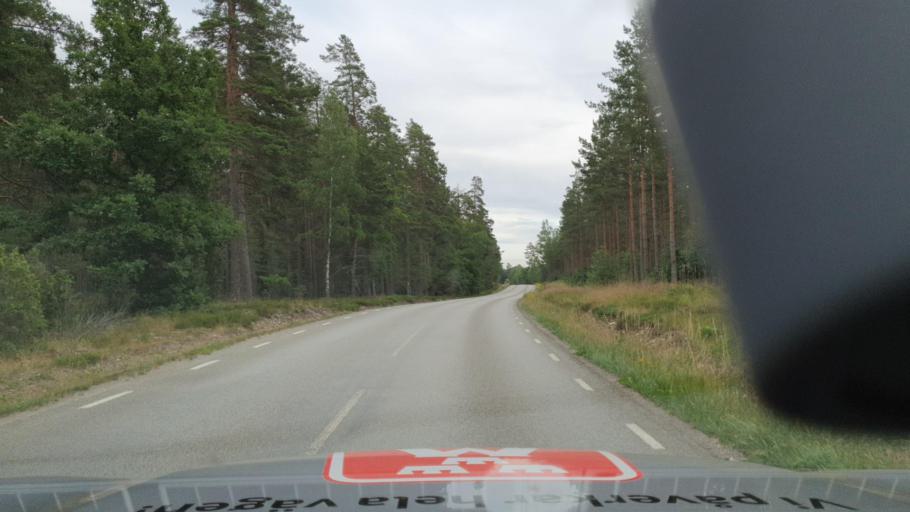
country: SE
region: Kalmar
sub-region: Kalmar Kommun
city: Trekanten
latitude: 56.6426
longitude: 16.0217
